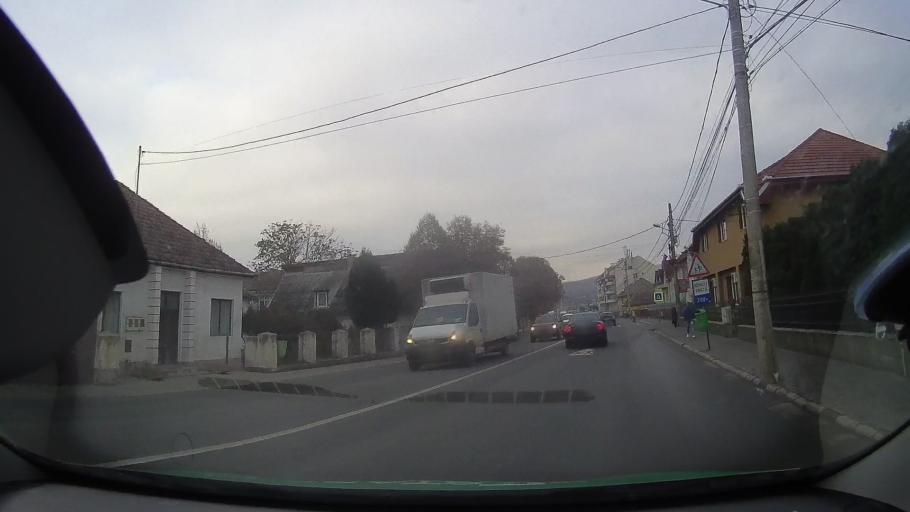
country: RO
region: Mures
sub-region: Comuna Ludus
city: Ludus
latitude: 46.4850
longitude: 24.0954
